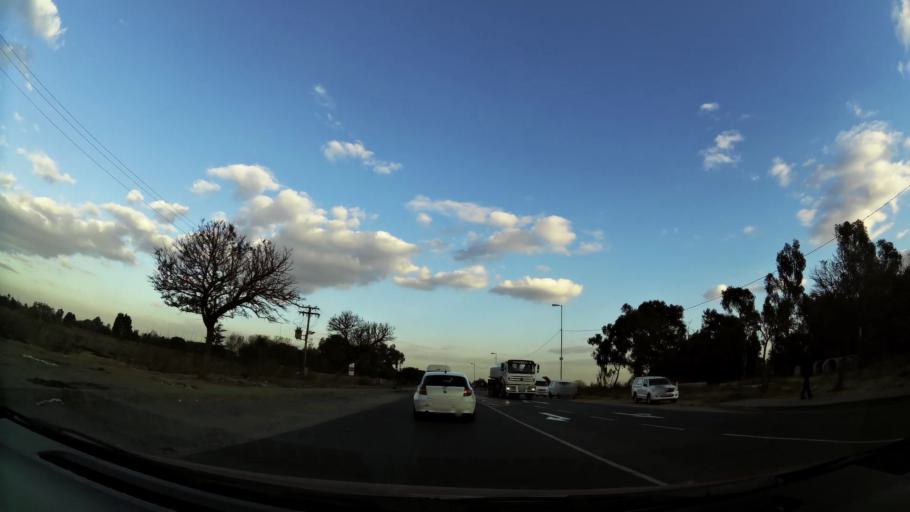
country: ZA
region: Gauteng
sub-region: City of Johannesburg Metropolitan Municipality
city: Midrand
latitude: -25.9894
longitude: 28.1532
